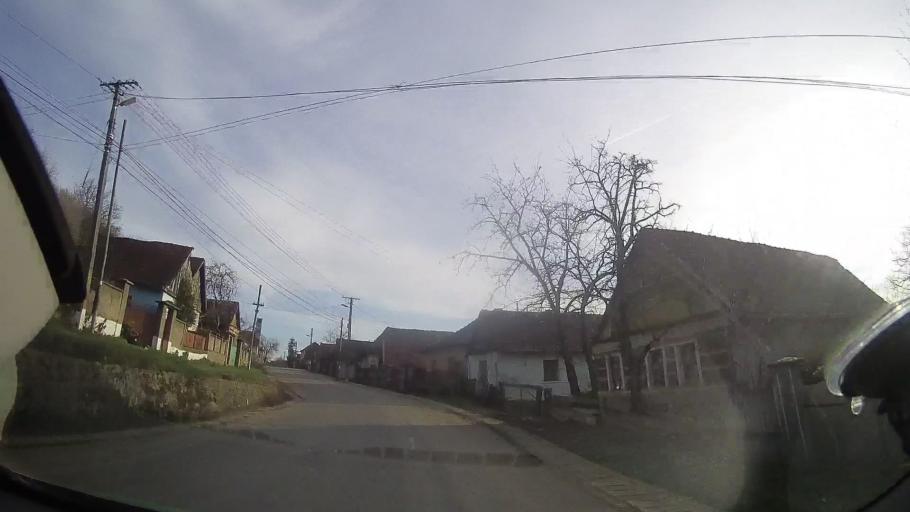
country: RO
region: Bihor
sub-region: Comuna Sarbi
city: Burzuc
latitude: 47.1519
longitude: 22.1727
